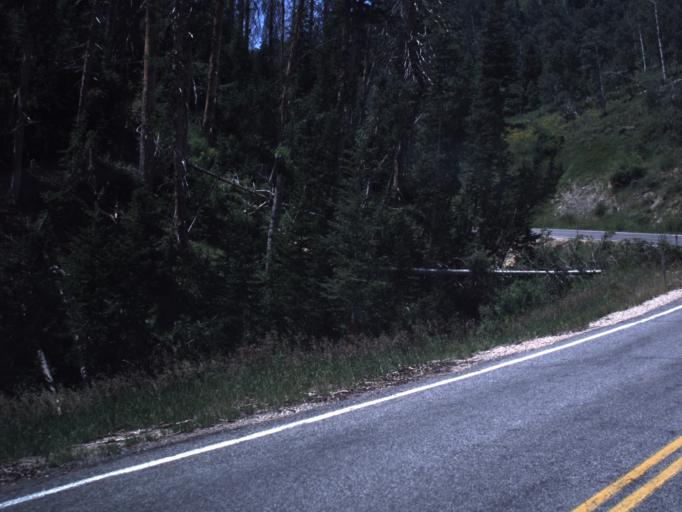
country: US
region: Utah
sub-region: Sanpete County
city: Fairview
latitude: 39.6487
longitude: -111.2549
